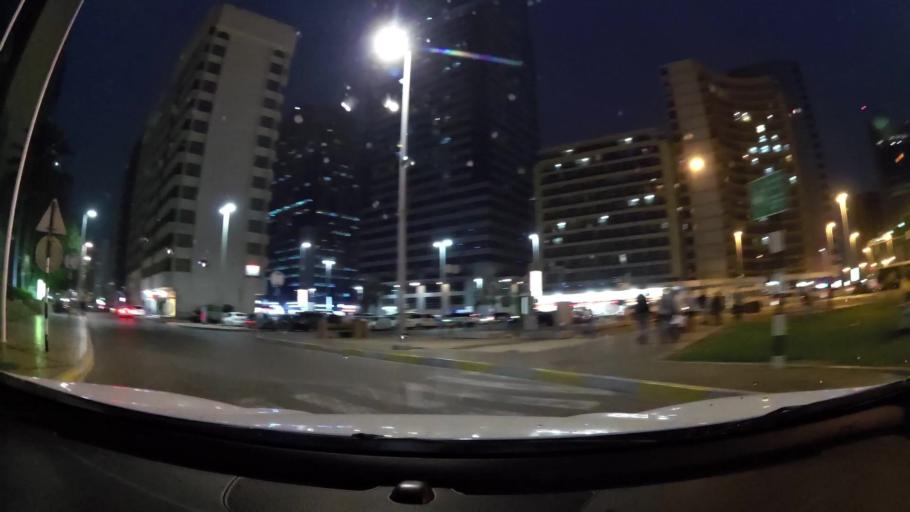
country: AE
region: Abu Dhabi
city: Abu Dhabi
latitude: 24.4836
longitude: 54.3592
